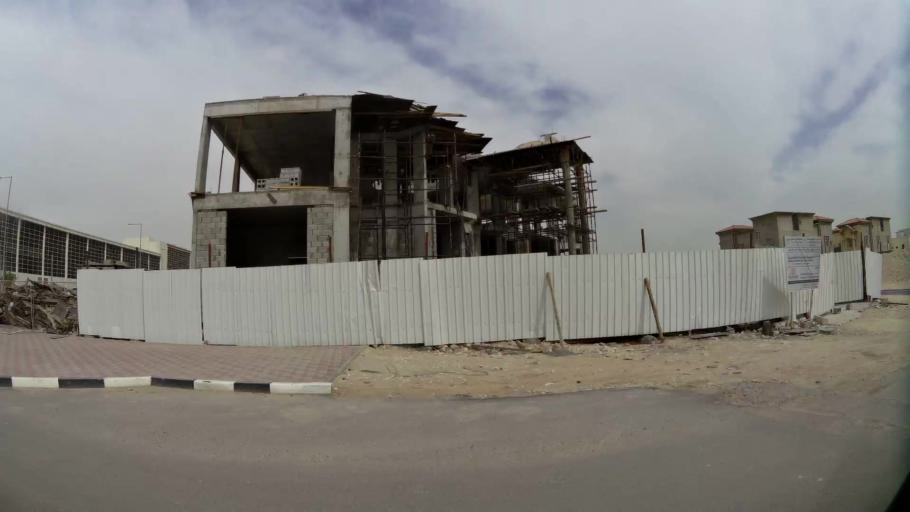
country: QA
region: Baladiyat ar Rayyan
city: Ar Rayyan
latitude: 25.2002
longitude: 51.4518
